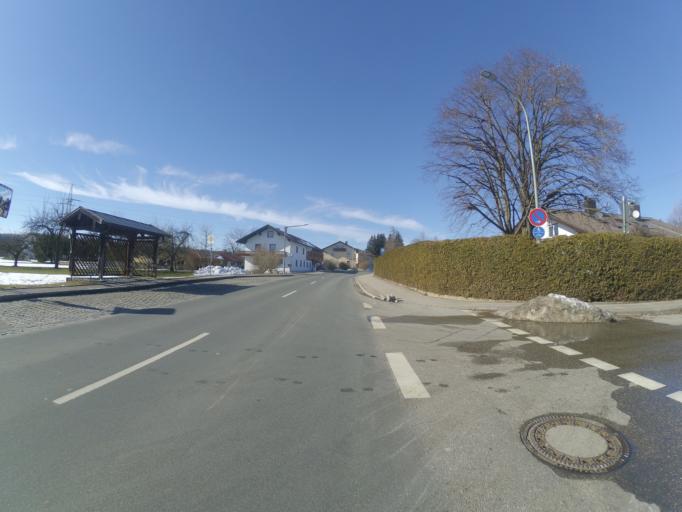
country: DE
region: Bavaria
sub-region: Upper Bavaria
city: Feldkirchen-Westerham
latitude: 47.8934
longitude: 11.8548
